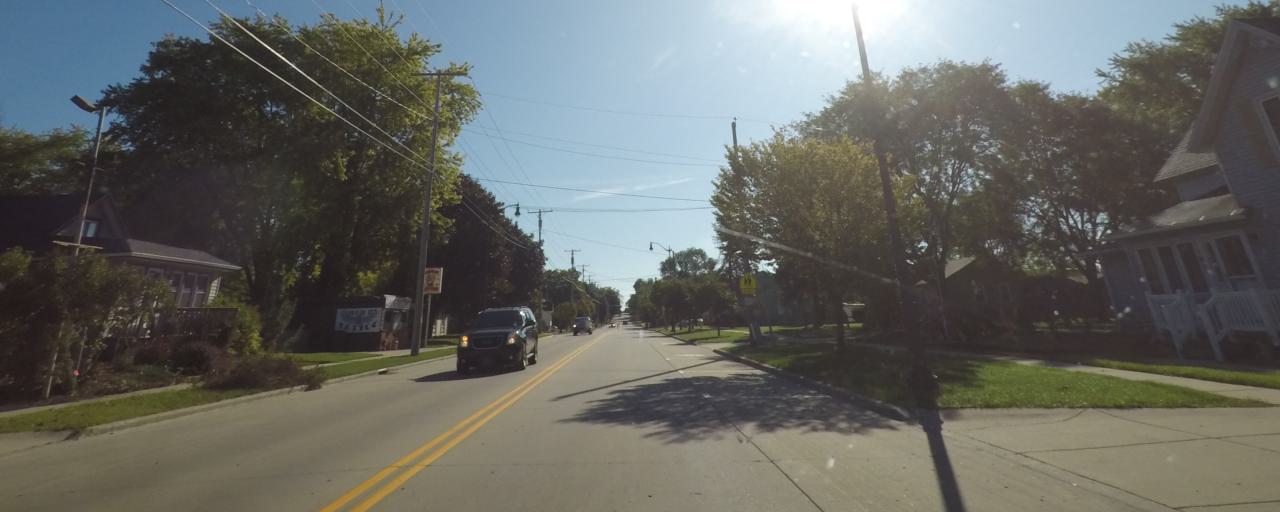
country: US
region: Wisconsin
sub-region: Jefferson County
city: Jefferson
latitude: 43.0058
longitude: -88.8200
